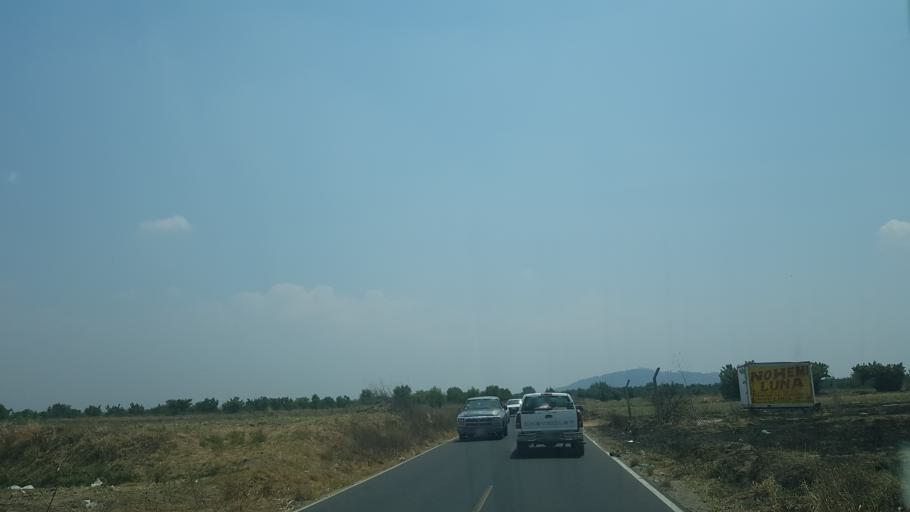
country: MX
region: Puebla
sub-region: San Jeronimo Tecuanipan
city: San Miguel Papaxtla
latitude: 19.0944
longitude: -98.4024
